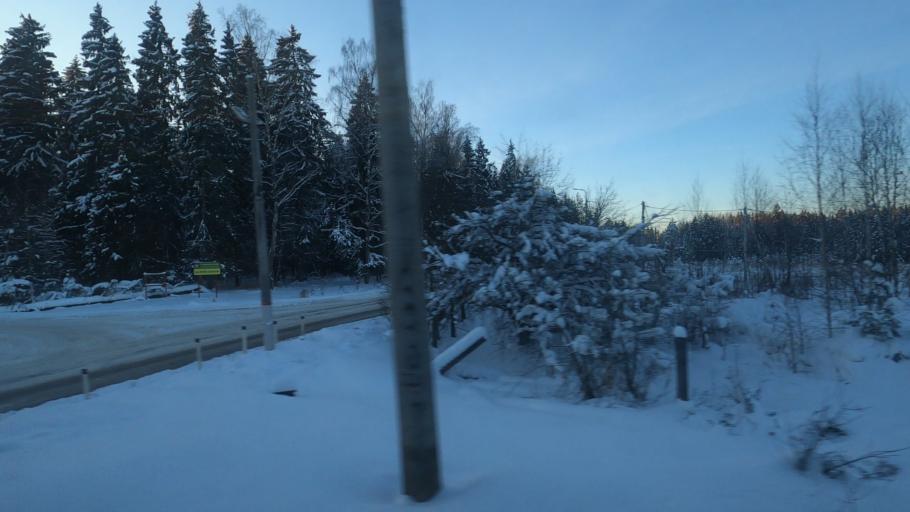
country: RU
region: Moskovskaya
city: Novo-Nikol'skoye
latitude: 56.5466
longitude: 37.5599
